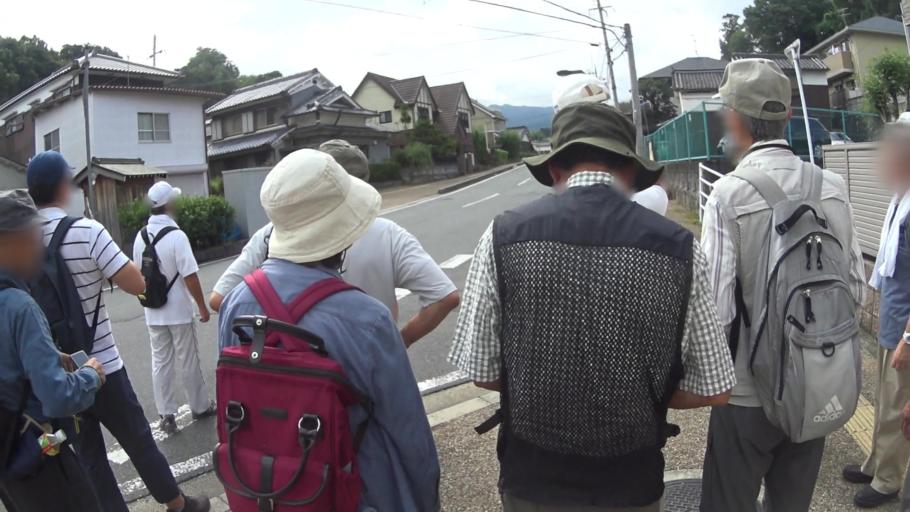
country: JP
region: Nara
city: Sakurai
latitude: 34.5086
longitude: 135.8465
